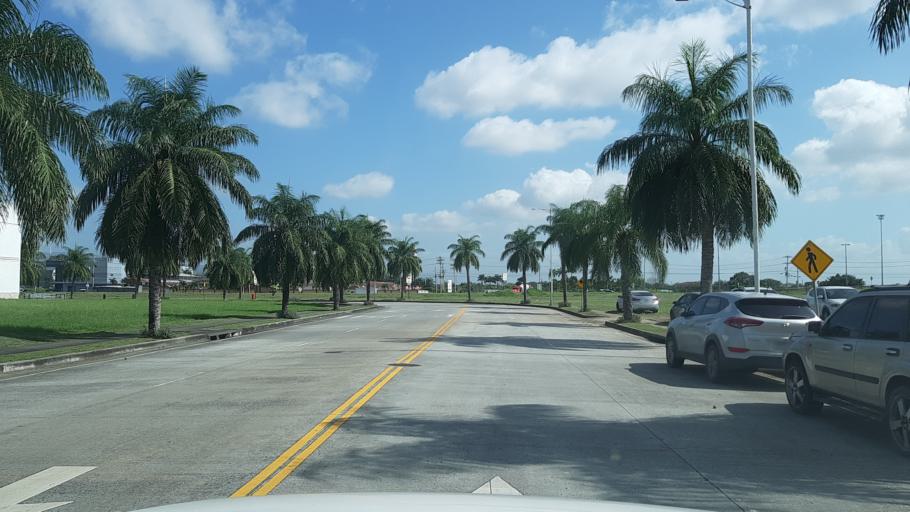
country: PA
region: Panama
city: San Miguelito
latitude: 9.0298
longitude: -79.4579
